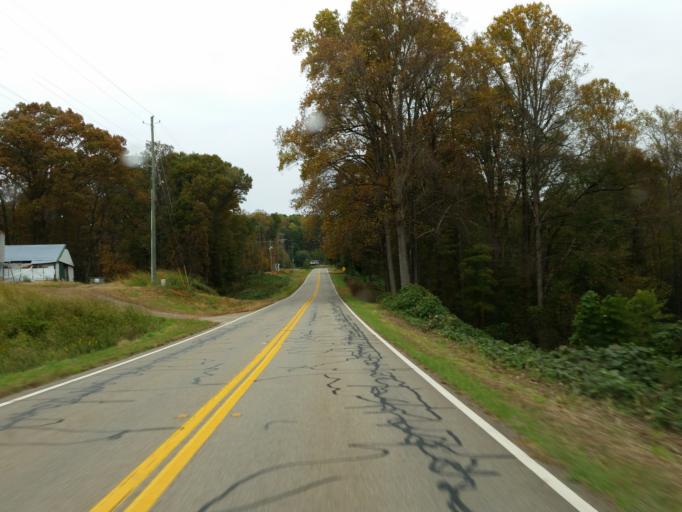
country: US
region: Georgia
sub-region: Pickens County
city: Jasper
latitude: 34.5218
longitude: -84.4176
